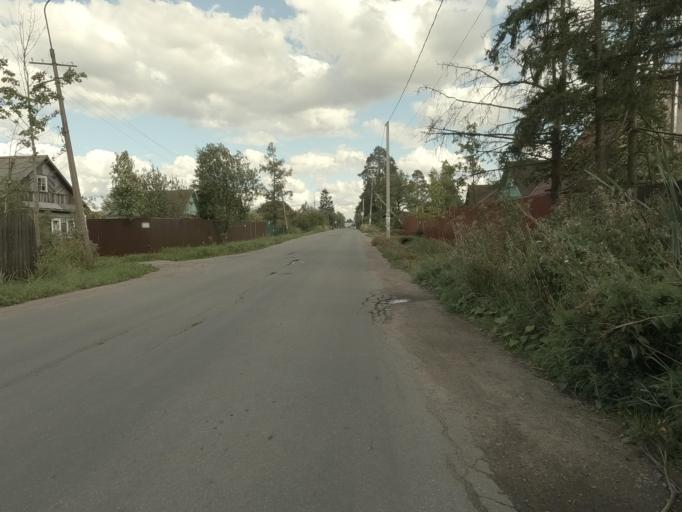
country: RU
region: Leningrad
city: Ul'yanovka
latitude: 59.6336
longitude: 30.7753
